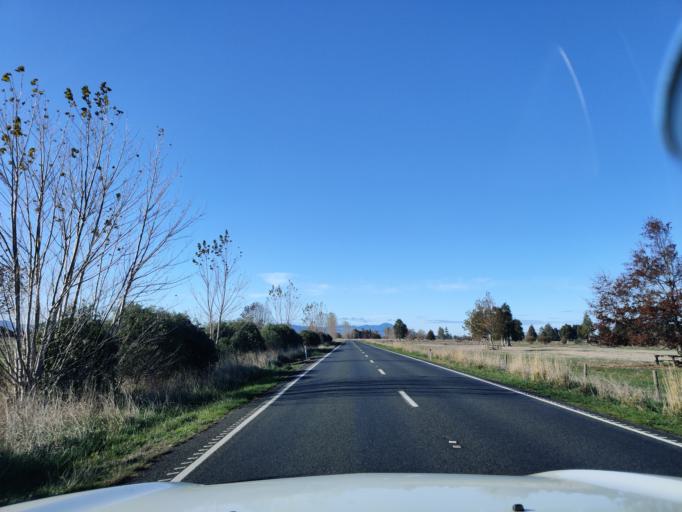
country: NZ
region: Waikato
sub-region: Hauraki District
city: Ngatea
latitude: -37.3038
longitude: 175.5608
